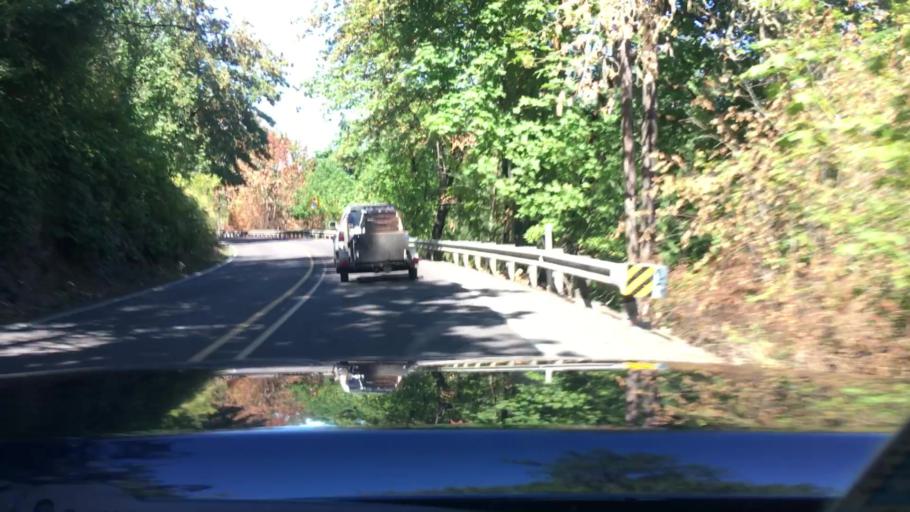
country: US
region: Oregon
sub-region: Lane County
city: Cottage Grove
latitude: 43.8258
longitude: -123.0448
